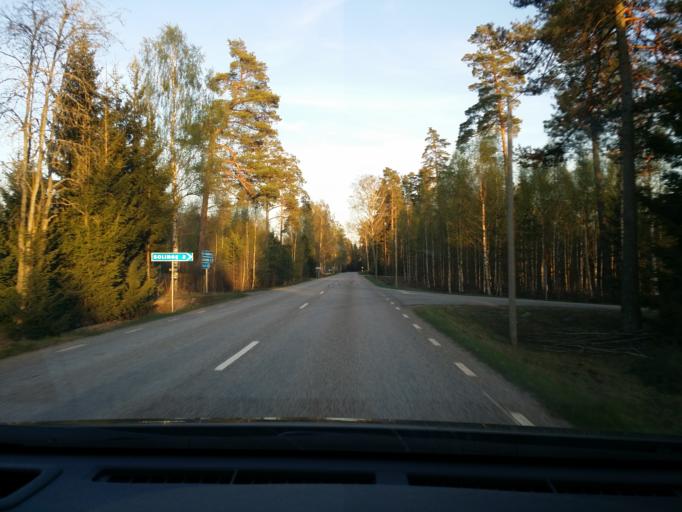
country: SE
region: Vaestmanland
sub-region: Sala Kommun
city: Sala
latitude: 59.8278
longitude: 16.5184
